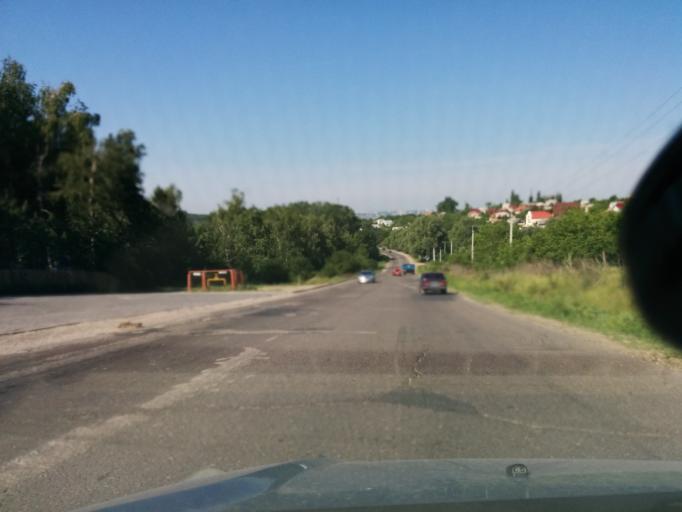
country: MD
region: Chisinau
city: Stauceni
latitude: 47.0571
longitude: 28.9445
